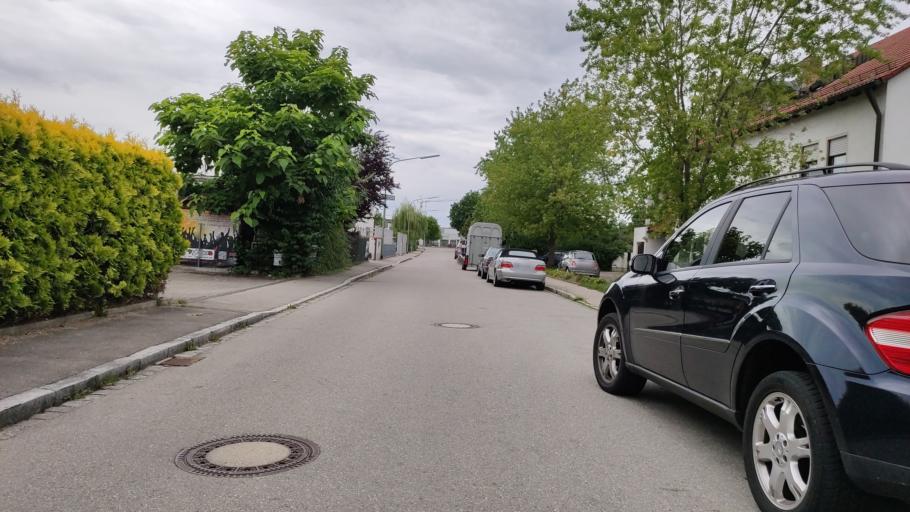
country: DE
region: Bavaria
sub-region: Swabia
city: Konigsbrunn
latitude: 48.2537
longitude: 10.8744
